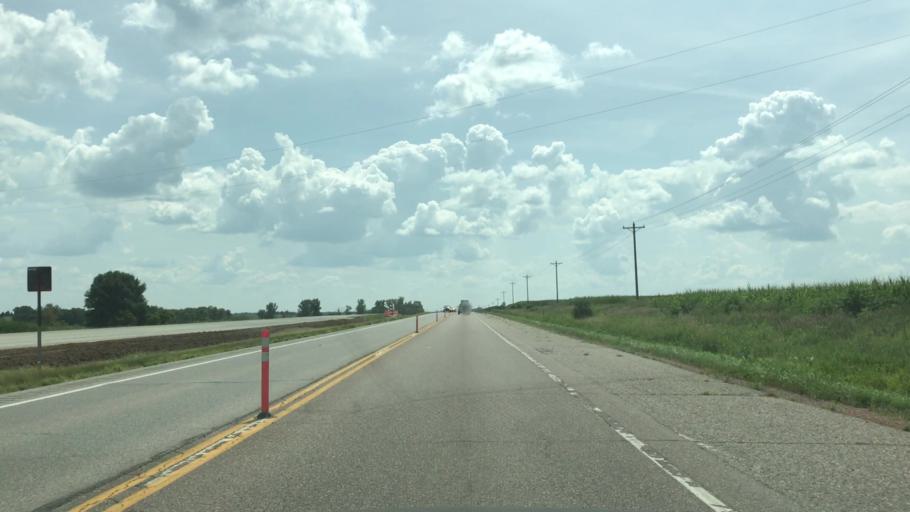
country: US
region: Minnesota
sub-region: Scott County
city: Belle Plaine
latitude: 44.5704
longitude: -93.8440
